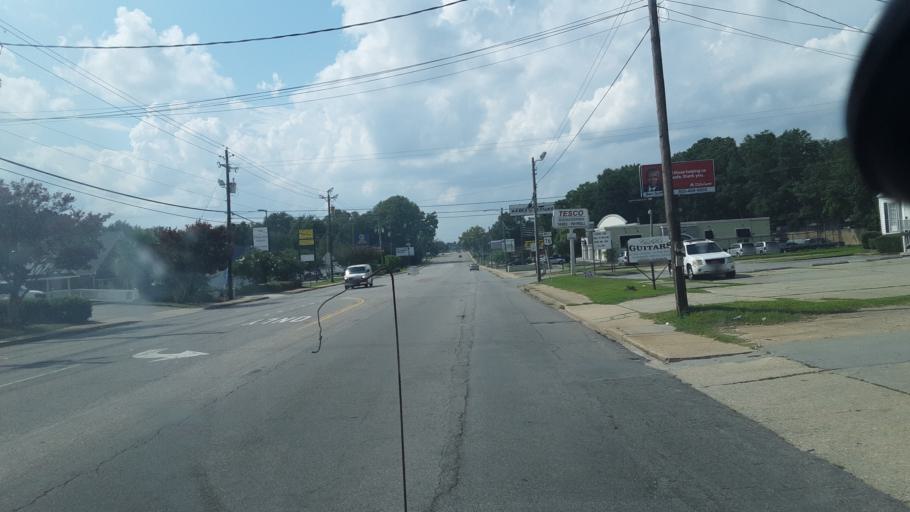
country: US
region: South Carolina
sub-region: Sumter County
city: Sumter
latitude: 33.9381
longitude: -80.3611
